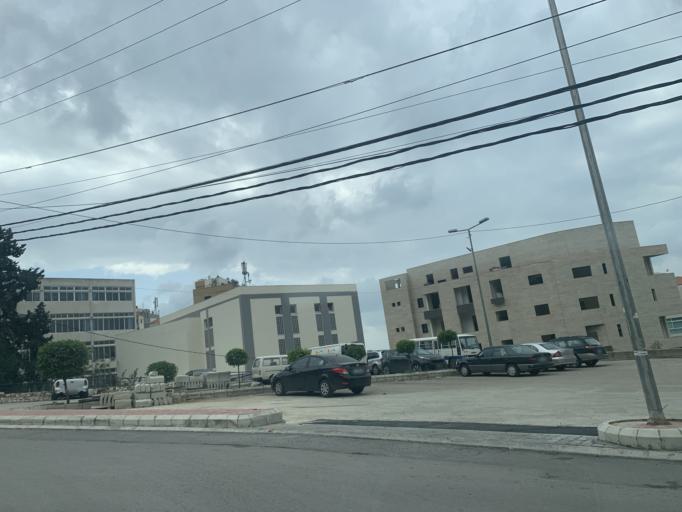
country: LB
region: Mont-Liban
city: Djounie
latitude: 33.9880
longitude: 35.6438
